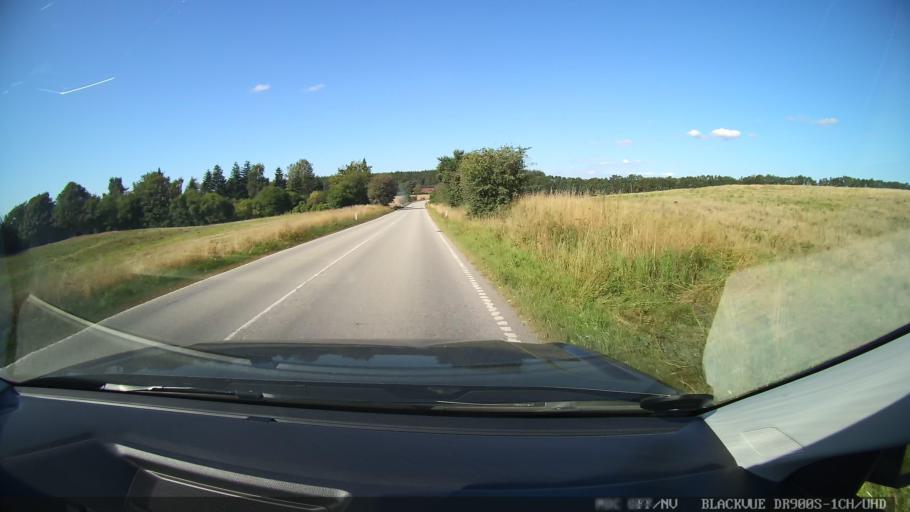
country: DK
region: North Denmark
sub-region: Mariagerfjord Kommune
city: Mariager
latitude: 56.6259
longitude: 9.9804
